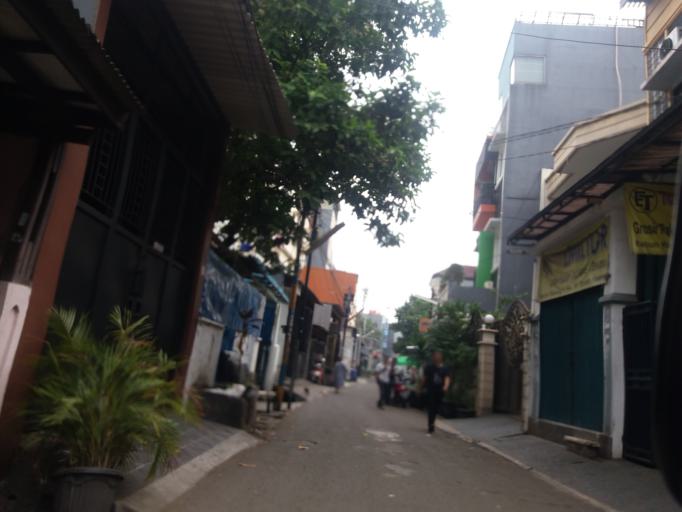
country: ID
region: Jakarta Raya
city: Jakarta
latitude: -6.1902
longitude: 106.8170
